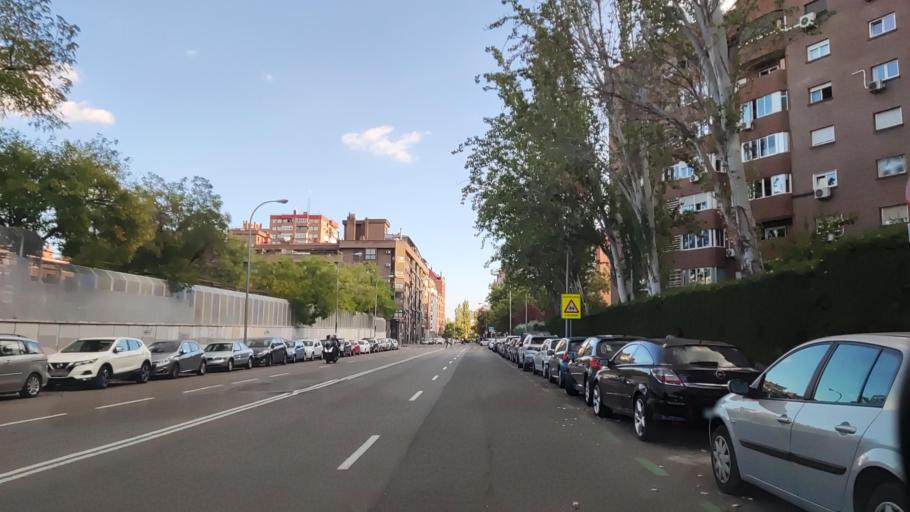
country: ES
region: Madrid
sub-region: Provincia de Madrid
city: Arganzuela
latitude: 40.3995
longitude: -3.7057
